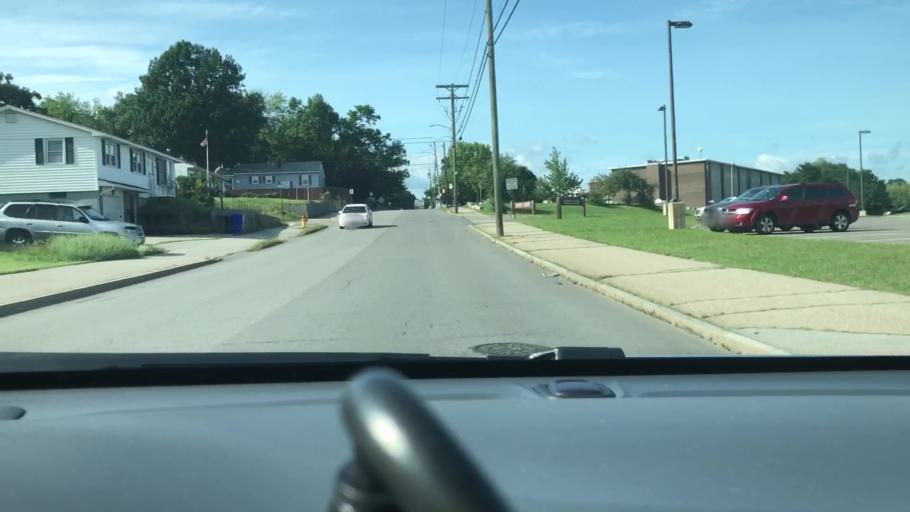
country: US
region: New Hampshire
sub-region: Hillsborough County
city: Manchester
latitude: 42.9661
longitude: -71.4374
